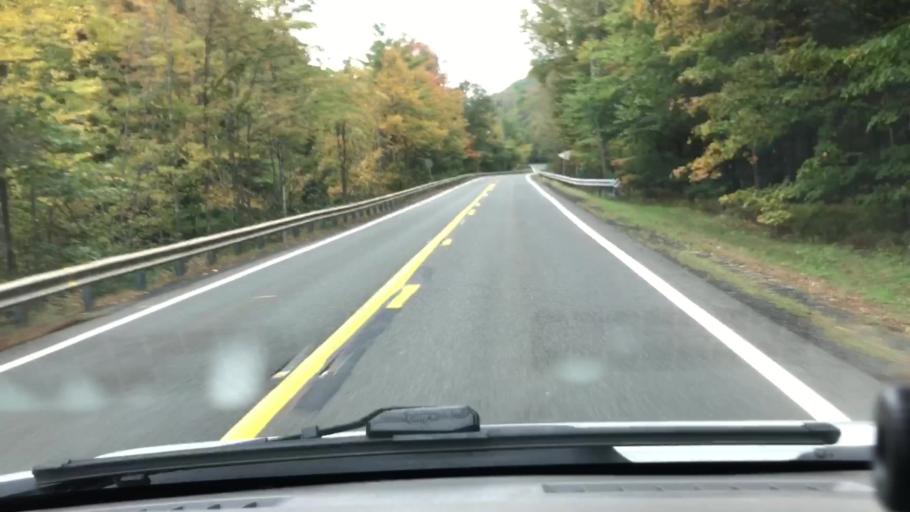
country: US
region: Massachusetts
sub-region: Hampshire County
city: Chesterfield
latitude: 42.3344
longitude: -72.8834
